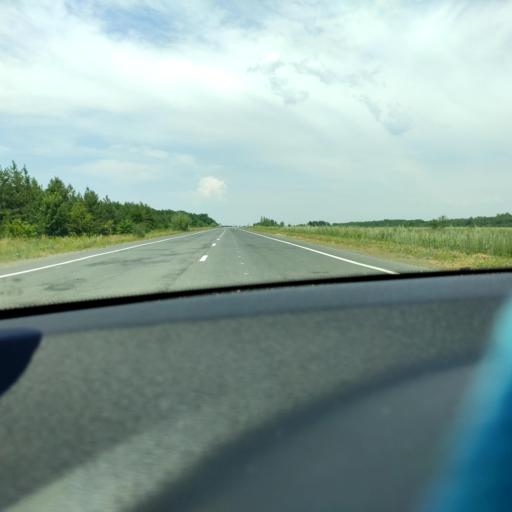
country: RU
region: Samara
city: Petra-Dubrava
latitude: 53.3258
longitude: 50.4273
